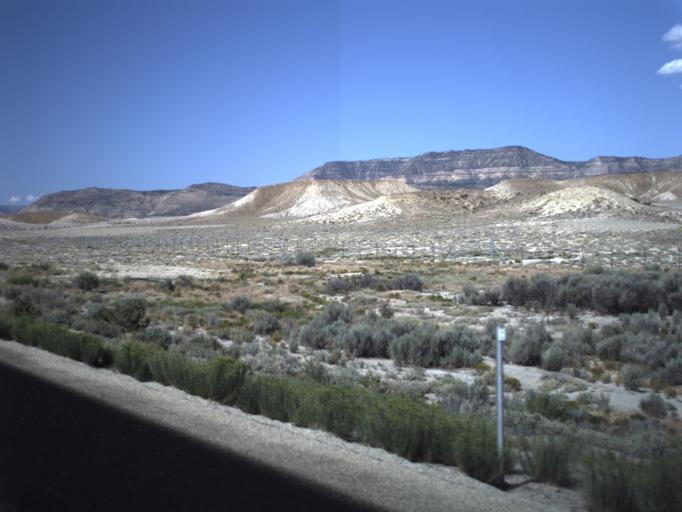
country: US
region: Utah
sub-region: Emery County
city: Ferron
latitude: 38.9730
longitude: -111.1796
